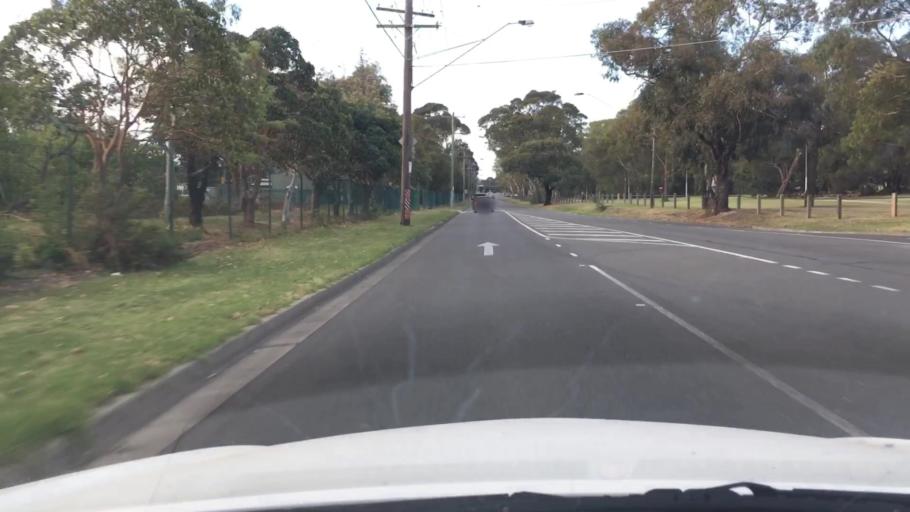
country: AU
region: Victoria
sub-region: Greater Dandenong
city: Noble Park
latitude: -37.9547
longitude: 145.1704
